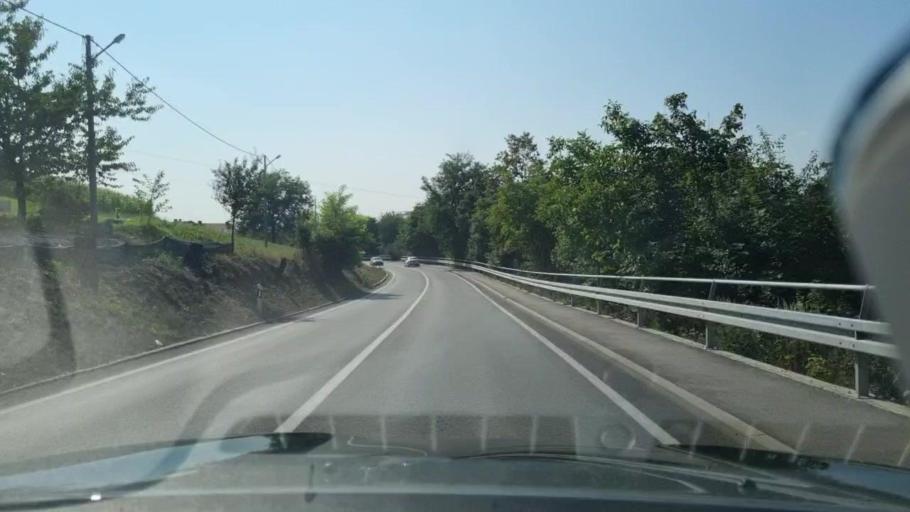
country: BA
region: Federation of Bosnia and Herzegovina
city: Cazin
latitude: 44.9657
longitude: 15.9172
